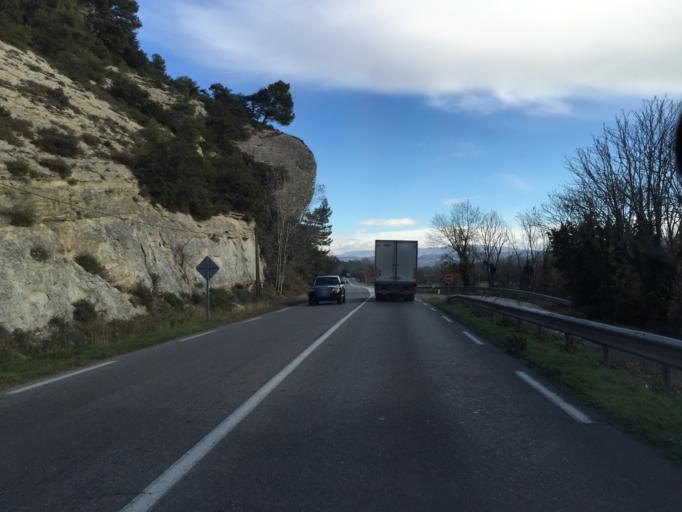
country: FR
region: Provence-Alpes-Cote d'Azur
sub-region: Departement du Vaucluse
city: Goult
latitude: 43.8594
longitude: 5.2275
